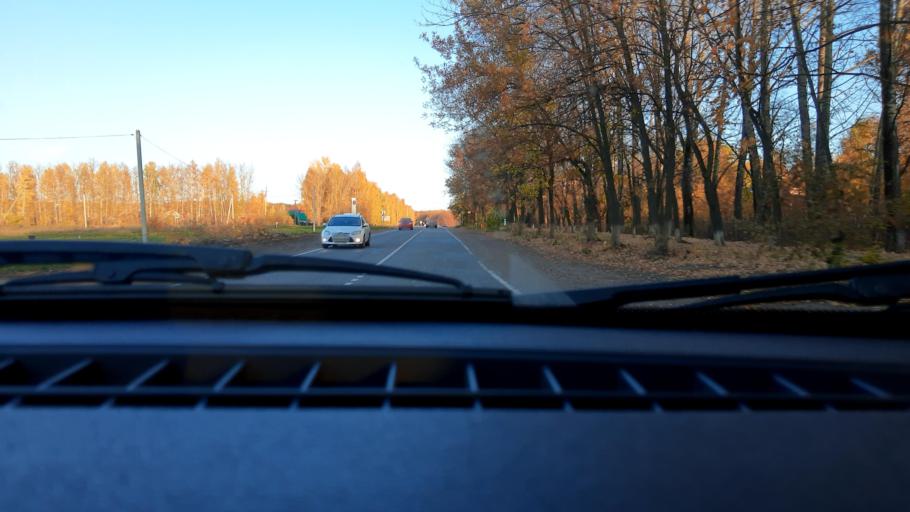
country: RU
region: Bashkortostan
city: Avdon
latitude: 54.8207
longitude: 55.6979
